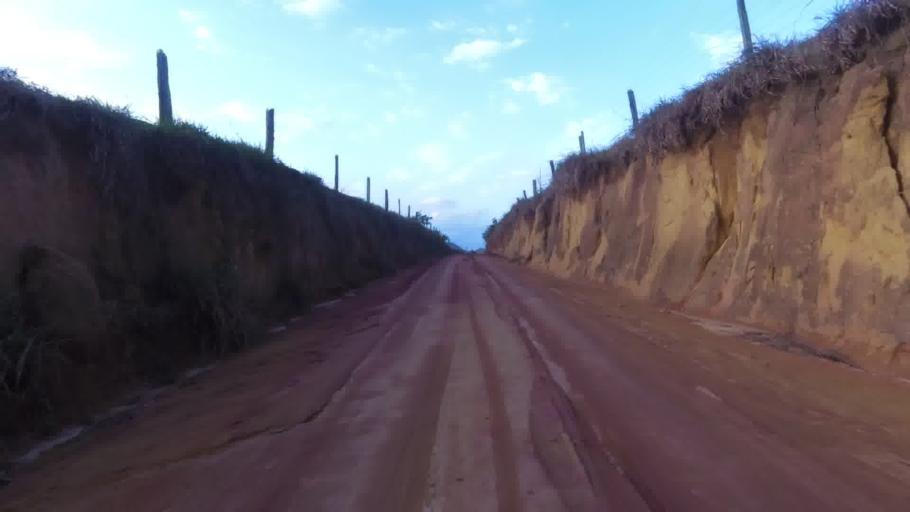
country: BR
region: Espirito Santo
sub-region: Alfredo Chaves
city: Alfredo Chaves
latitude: -20.7013
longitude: -40.6351
